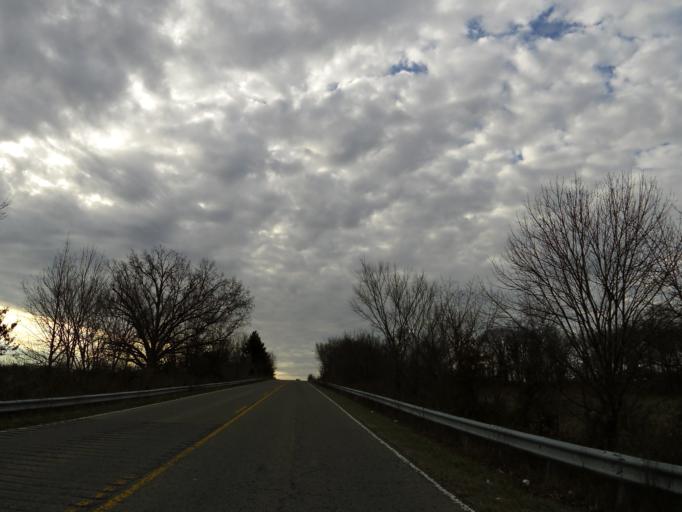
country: US
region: Illinois
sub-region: Jefferson County
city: Mount Vernon
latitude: 38.3748
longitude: -89.0346
